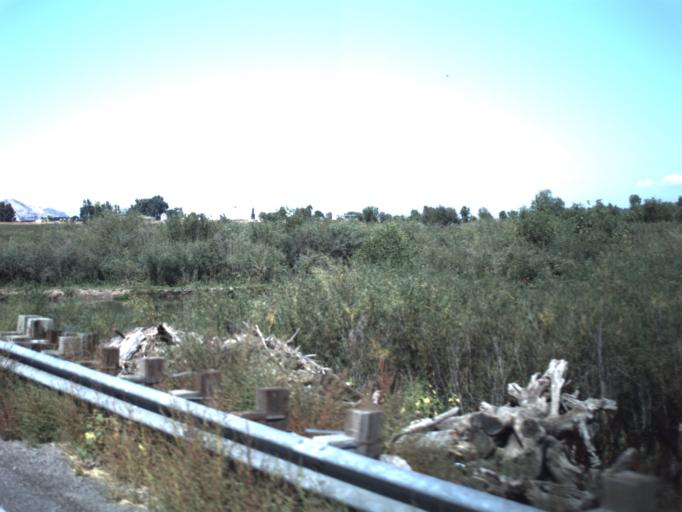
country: US
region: Utah
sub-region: Cache County
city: Smithfield
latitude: 41.8406
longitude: -111.8803
